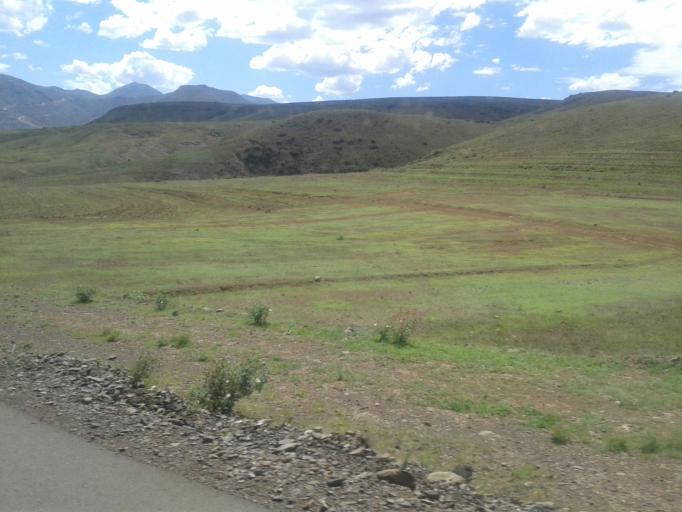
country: LS
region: Qacha's Nek
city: Qacha's Nek
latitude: -30.0232
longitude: 28.2169
